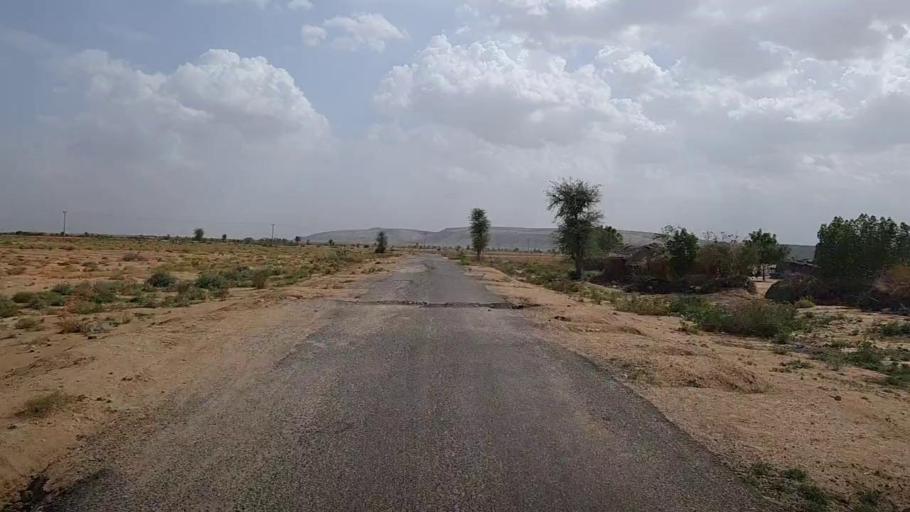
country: PK
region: Sindh
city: Jamshoro
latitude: 25.4016
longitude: 67.7674
